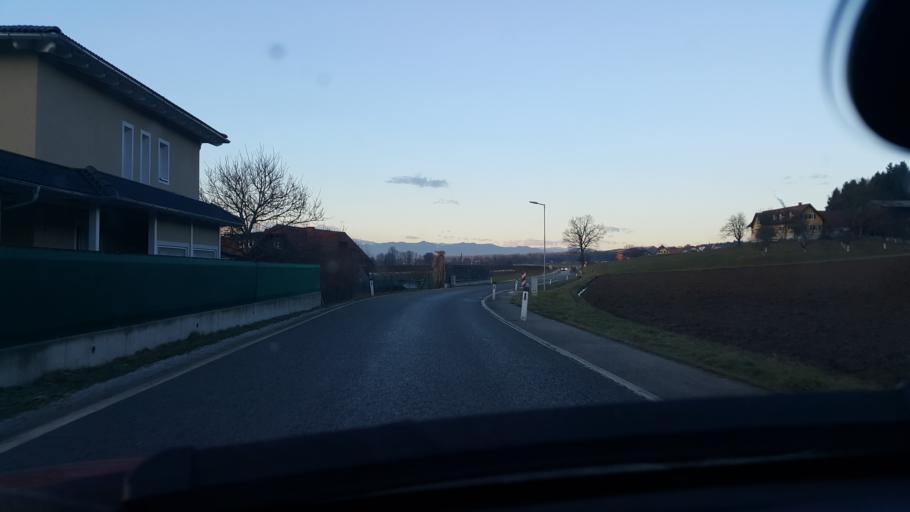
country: AT
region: Styria
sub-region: Politischer Bezirk Graz-Umgebung
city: Lieboch
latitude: 46.9806
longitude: 15.3427
